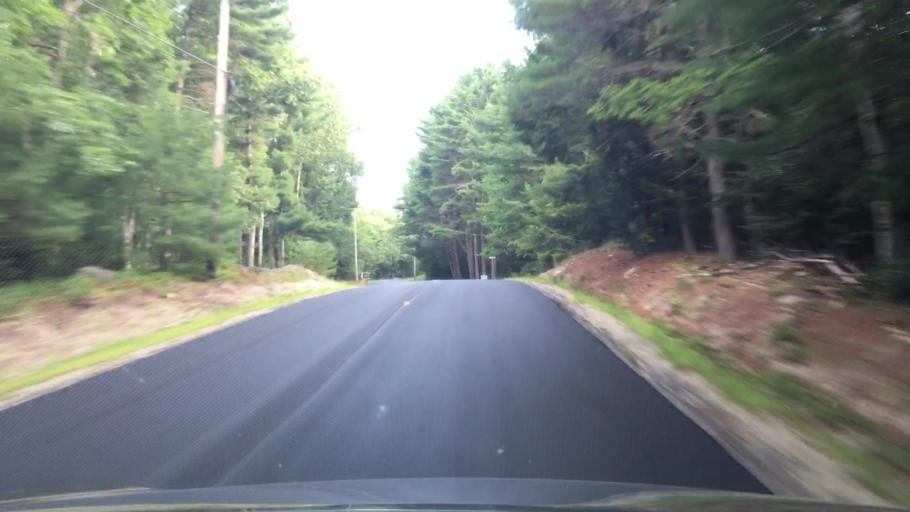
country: US
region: Maine
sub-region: Hancock County
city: Surry
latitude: 44.5240
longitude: -68.6091
